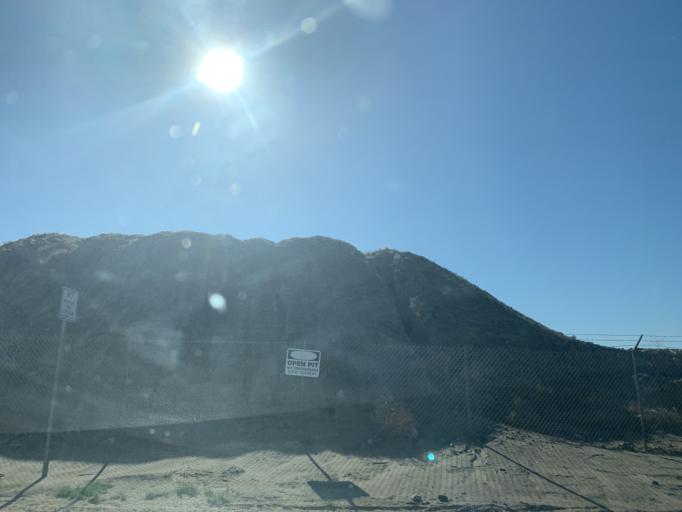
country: US
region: Arizona
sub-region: Maricopa County
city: Laveen
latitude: 33.4029
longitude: -112.1448
